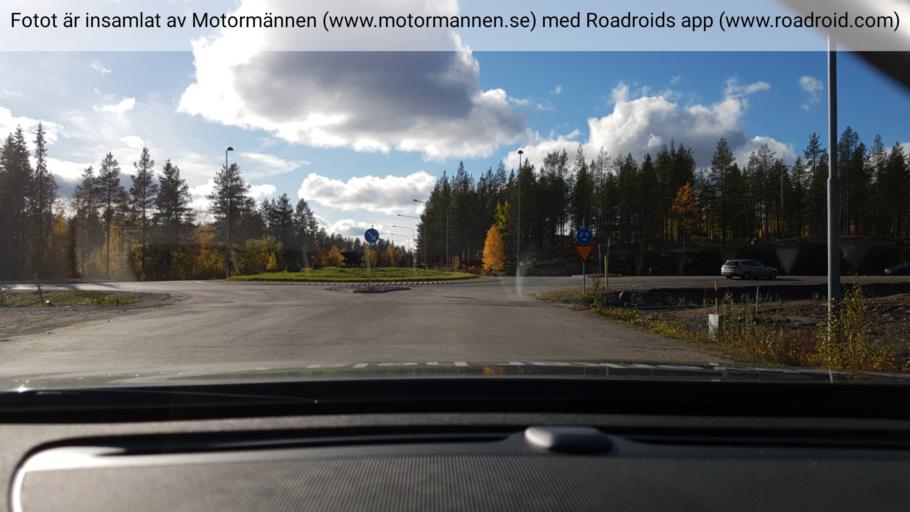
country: SE
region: Norrbotten
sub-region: Gallivare Kommun
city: Malmberget
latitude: 67.1653
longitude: 20.6497
